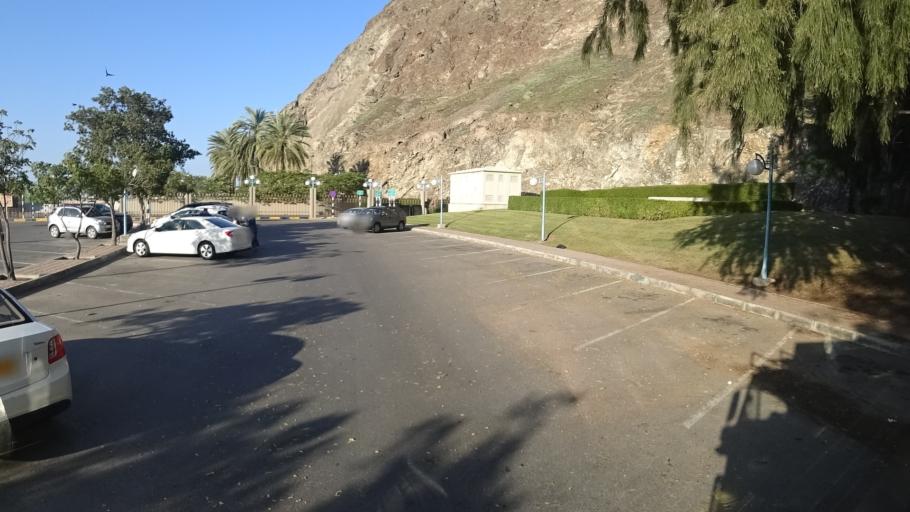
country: OM
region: Muhafazat Masqat
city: Muscat
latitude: 23.6215
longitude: 58.5850
